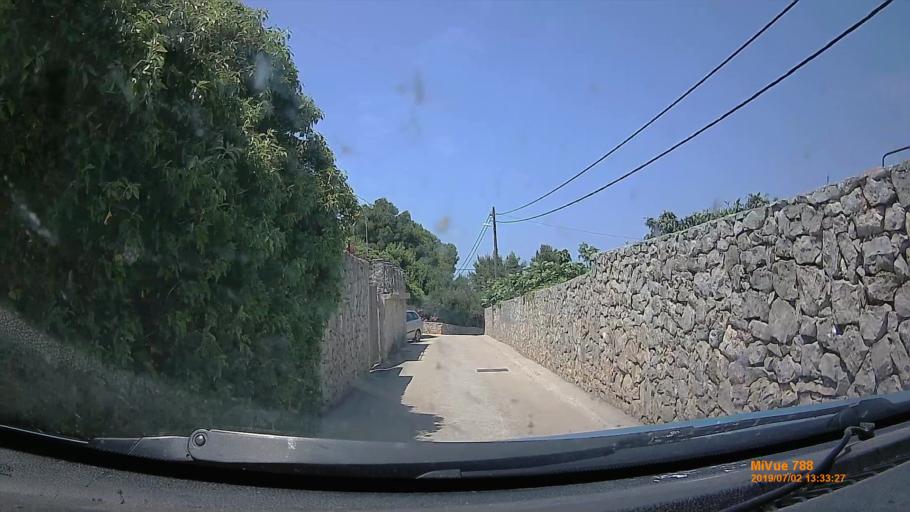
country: HR
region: Primorsko-Goranska
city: Mali Losinj
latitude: 44.5151
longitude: 14.5069
